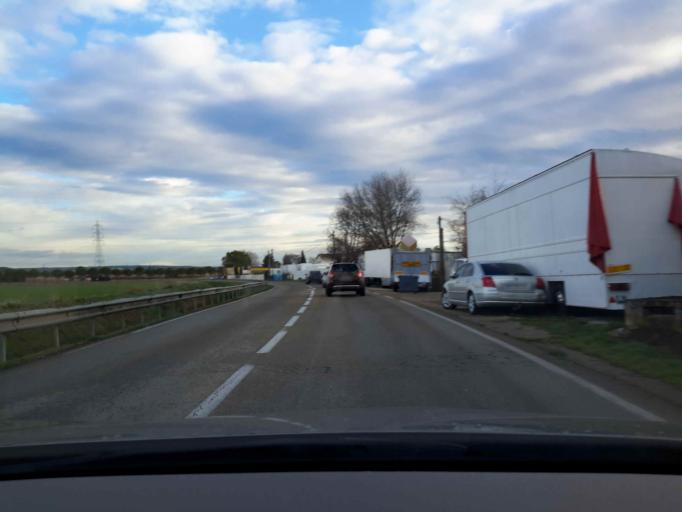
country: FR
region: Languedoc-Roussillon
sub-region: Departement du Gard
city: Caissargues
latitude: 43.7940
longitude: 4.3519
